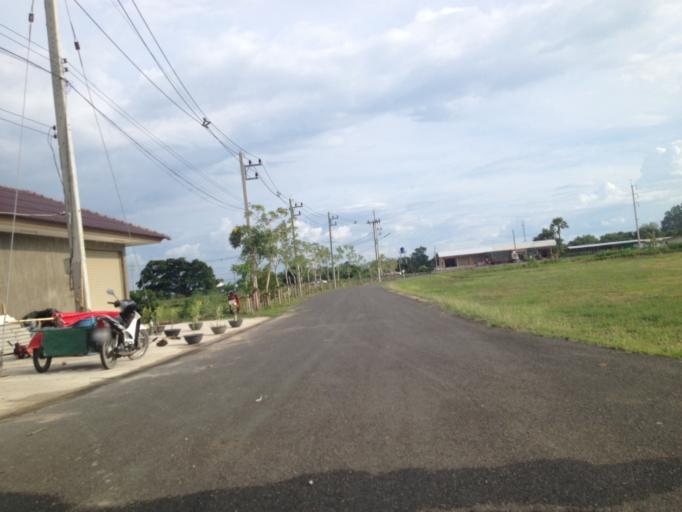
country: TH
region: Chiang Mai
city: Hang Dong
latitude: 18.7101
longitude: 98.9173
